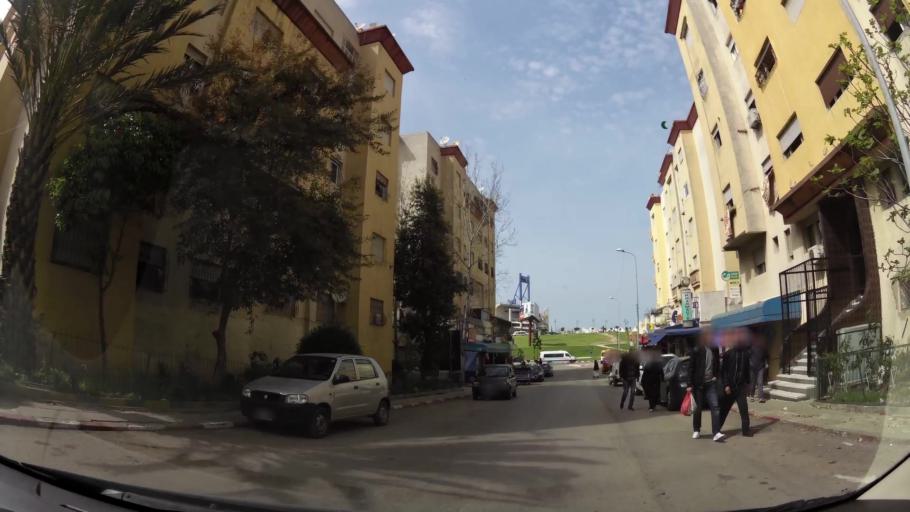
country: MA
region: Tanger-Tetouan
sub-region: Tanger-Assilah
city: Boukhalef
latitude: 35.7368
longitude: -5.8558
